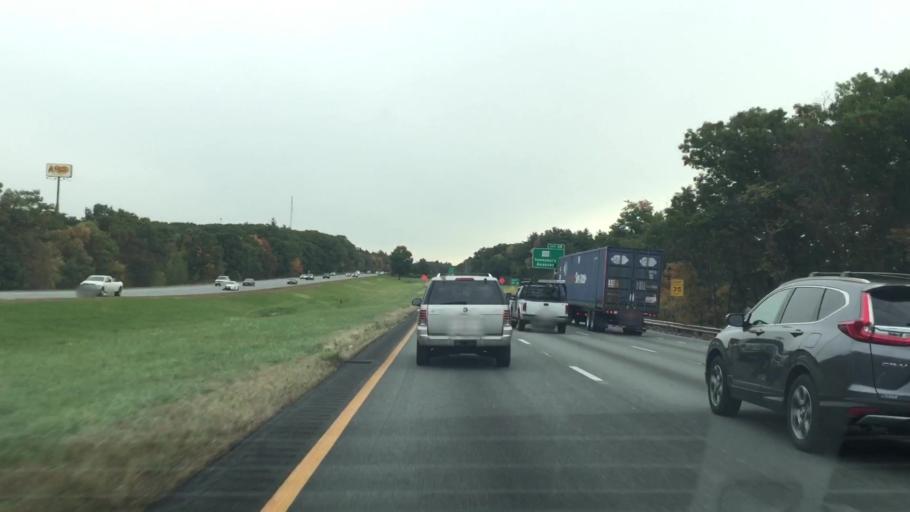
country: US
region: Massachusetts
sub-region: Middlesex County
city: Tewksbury
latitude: 42.6370
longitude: -71.2430
